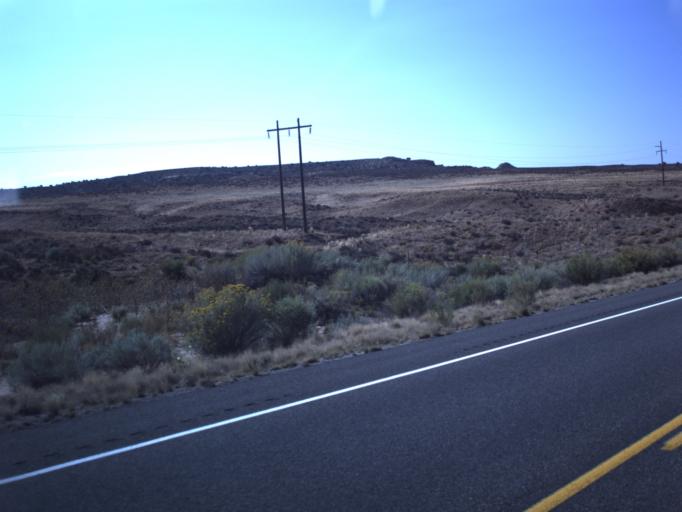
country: US
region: Utah
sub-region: San Juan County
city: Blanding
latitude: 37.3650
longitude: -109.5101
